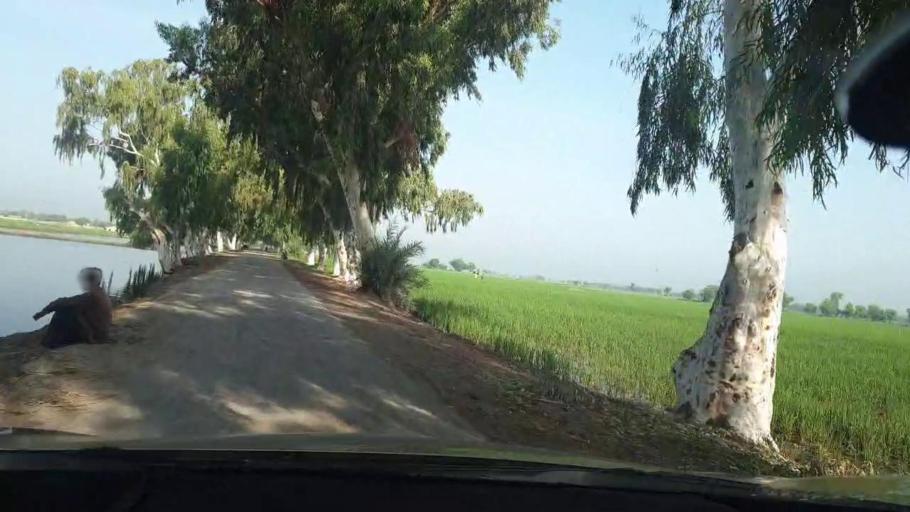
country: PK
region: Sindh
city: Kambar
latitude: 27.6509
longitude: 68.0397
